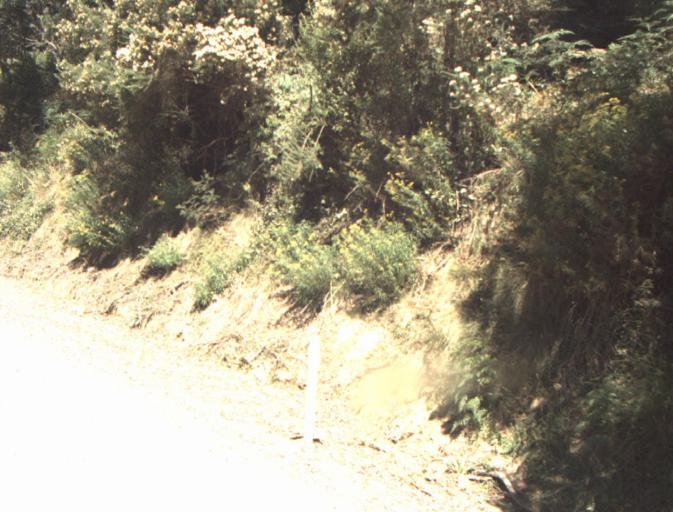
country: AU
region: Tasmania
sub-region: Dorset
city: Scottsdale
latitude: -41.3260
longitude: 147.4229
